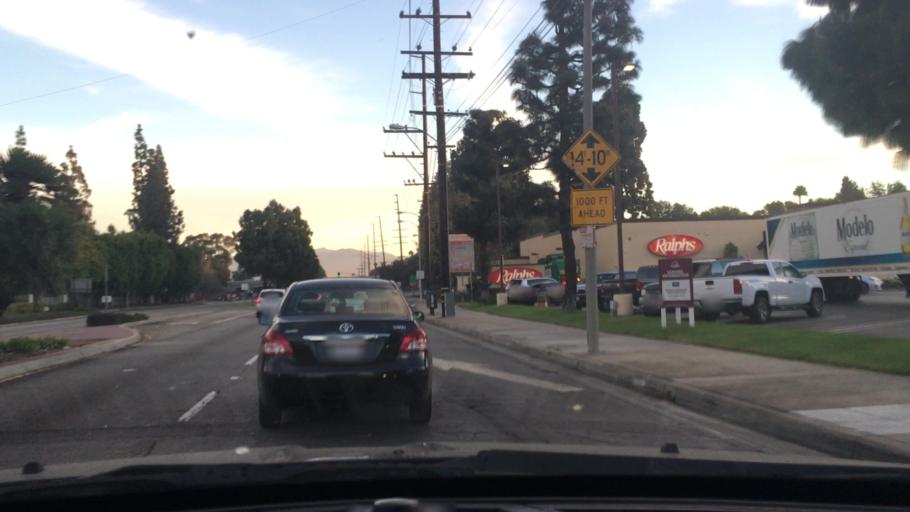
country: US
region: California
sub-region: Los Angeles County
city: Downey
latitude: 33.9550
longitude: -118.1132
